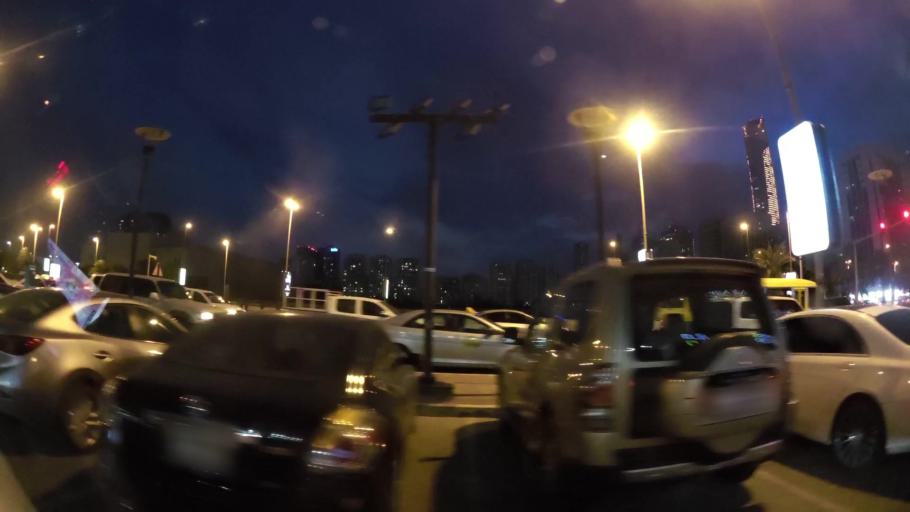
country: AE
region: Abu Dhabi
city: Abu Dhabi
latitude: 24.4846
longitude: 54.3584
